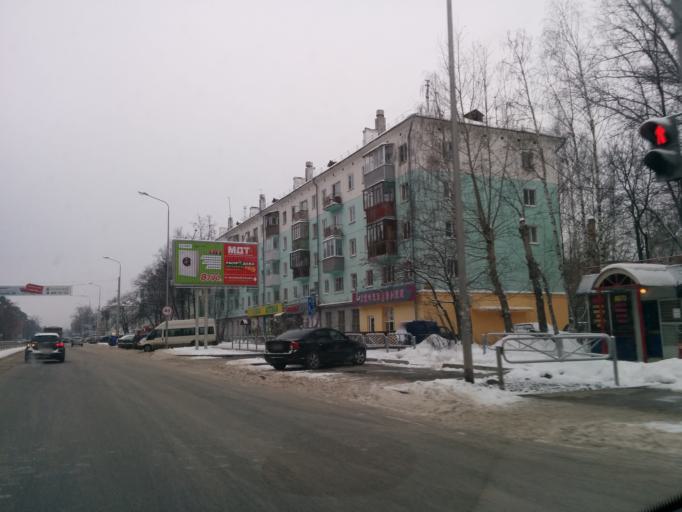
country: RU
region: Perm
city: Kultayevo
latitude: 58.0159
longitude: 55.9805
